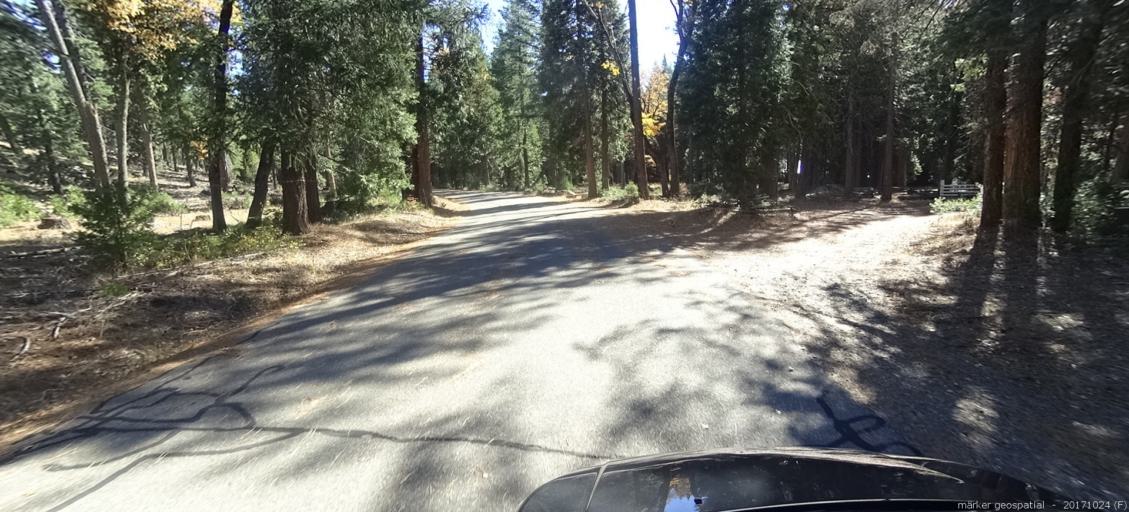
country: US
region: California
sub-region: Shasta County
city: Shingletown
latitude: 40.5033
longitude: -121.6623
